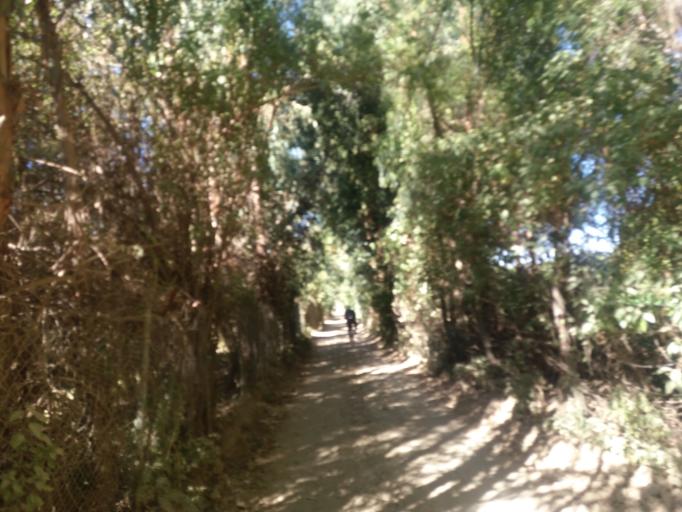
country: BO
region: Cochabamba
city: Cochabamba
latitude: -17.3460
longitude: -66.2173
